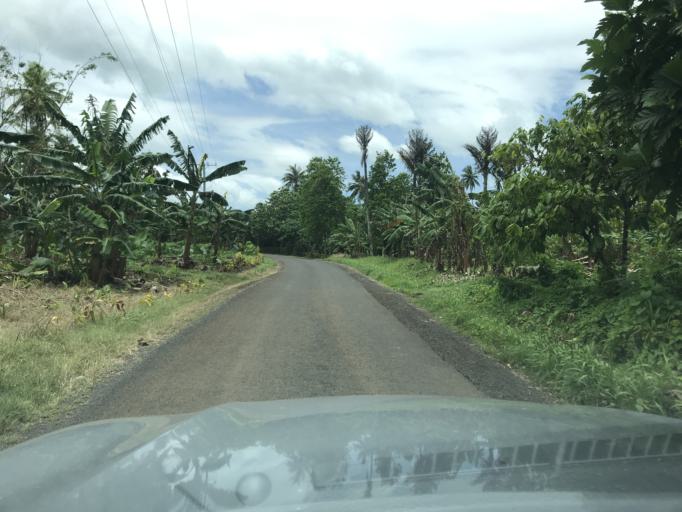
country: WS
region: Tuamasaga
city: Afenga
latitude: -13.8084
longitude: -171.8854
